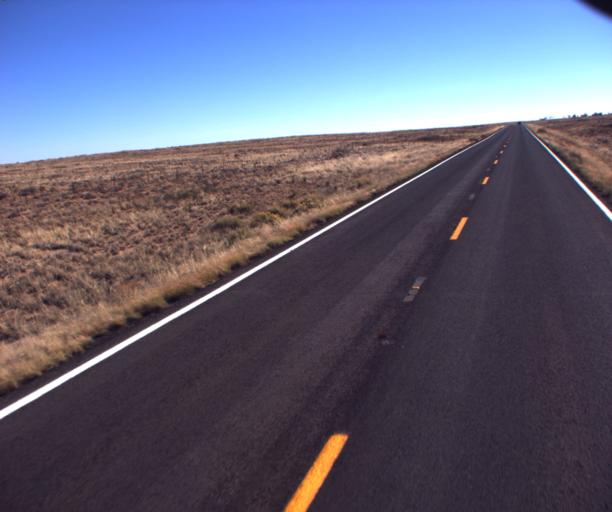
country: US
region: Arizona
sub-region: Coconino County
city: Tuba City
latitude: 35.9668
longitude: -110.9539
